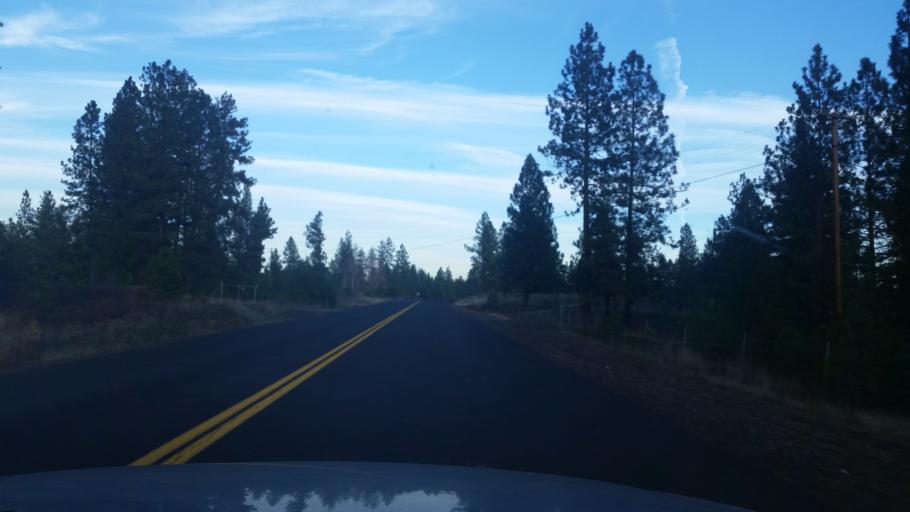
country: US
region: Washington
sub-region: Spokane County
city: Cheney
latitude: 47.4805
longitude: -117.5140
